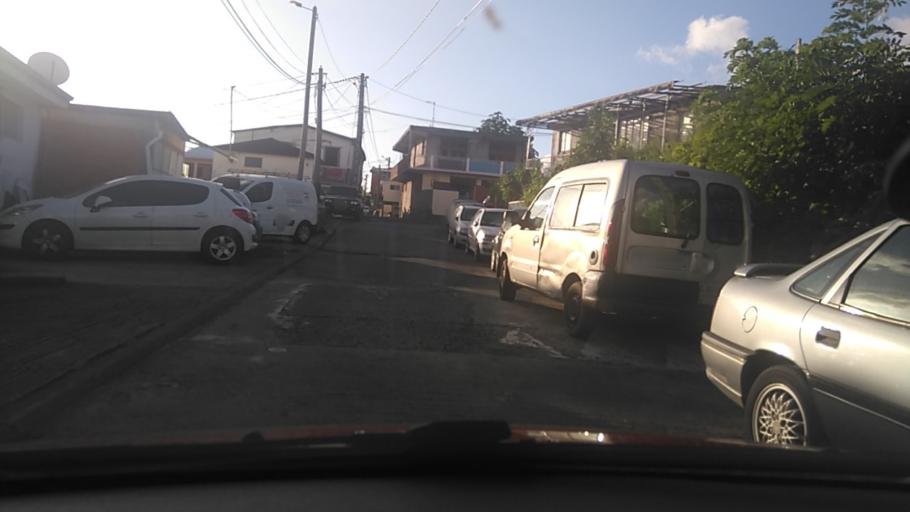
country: MQ
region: Martinique
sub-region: Martinique
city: Fort-de-France
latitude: 14.6027
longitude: -61.0926
